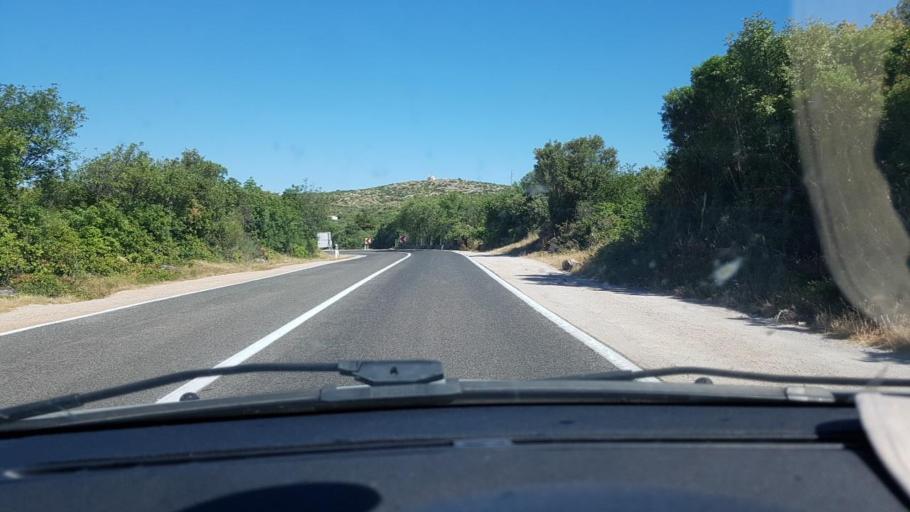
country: HR
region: Sibensko-Kniniska
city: Zaton
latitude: 43.7612
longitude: 15.8383
